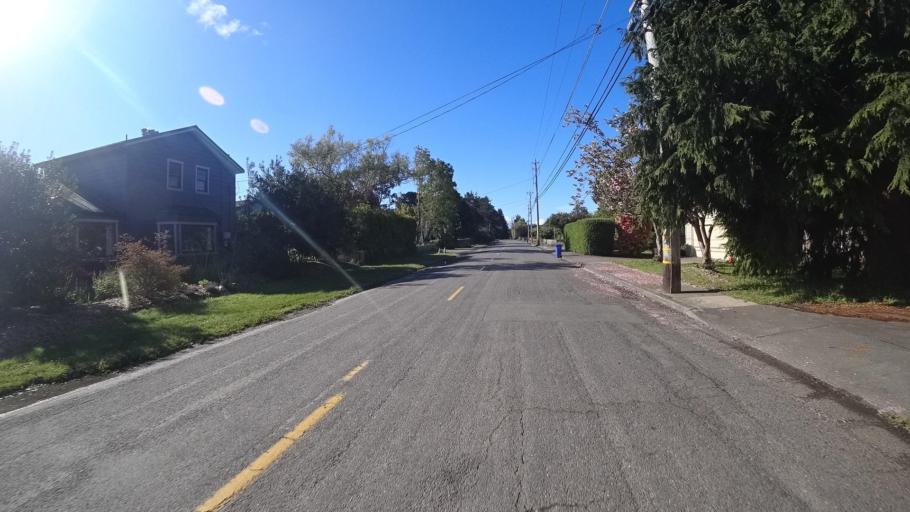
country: US
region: California
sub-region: Humboldt County
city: McKinleyville
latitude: 40.9724
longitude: -124.0959
